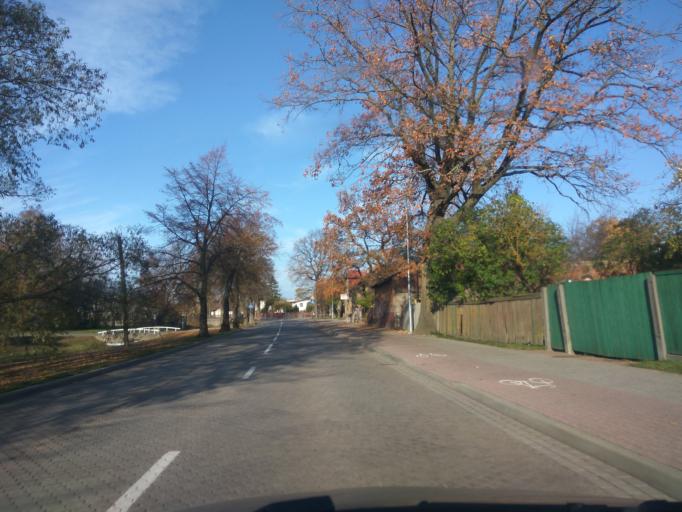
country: LV
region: Ventspils
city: Ventspils
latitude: 57.3772
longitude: 21.5734
